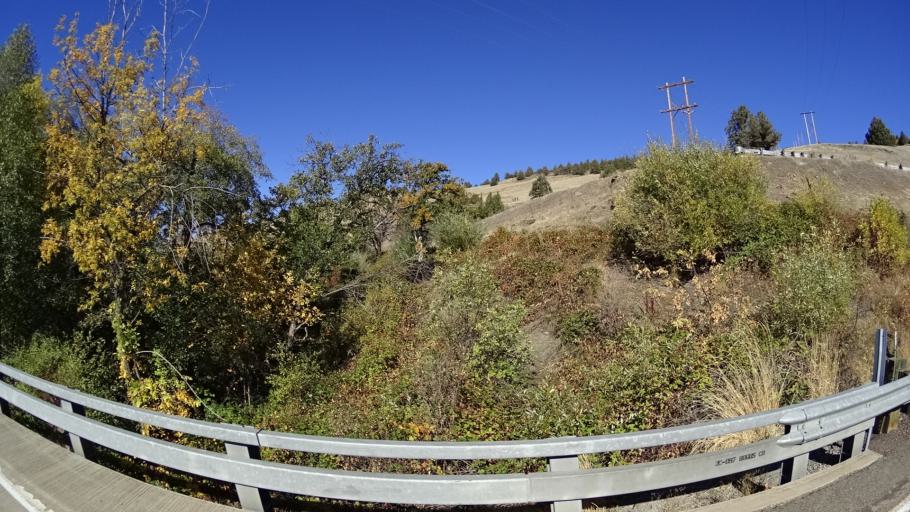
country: US
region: California
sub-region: Siskiyou County
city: Montague
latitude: 41.9277
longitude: -122.3657
